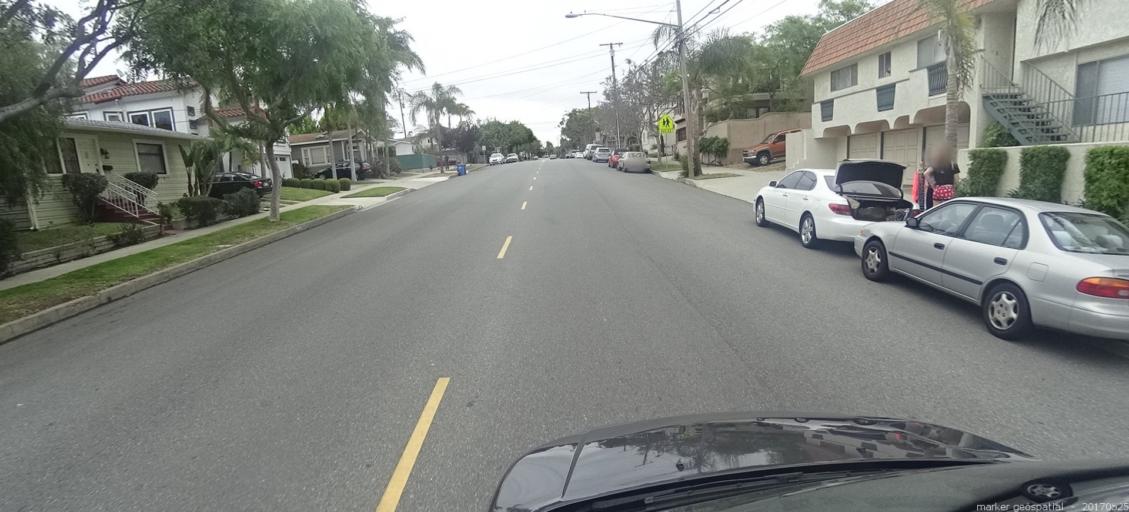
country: US
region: California
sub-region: Los Angeles County
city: Redondo Beach
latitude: 33.8424
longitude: -118.3801
